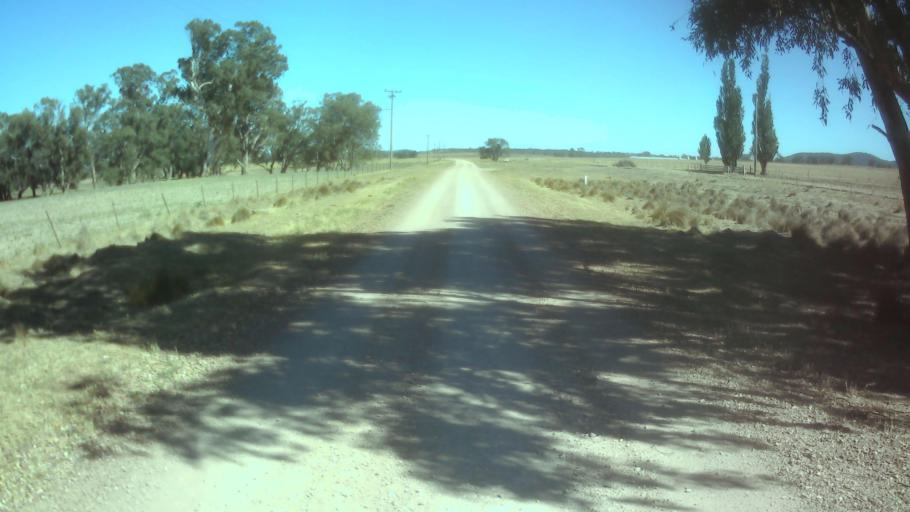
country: AU
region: New South Wales
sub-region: Weddin
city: Grenfell
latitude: -33.9417
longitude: 148.2902
